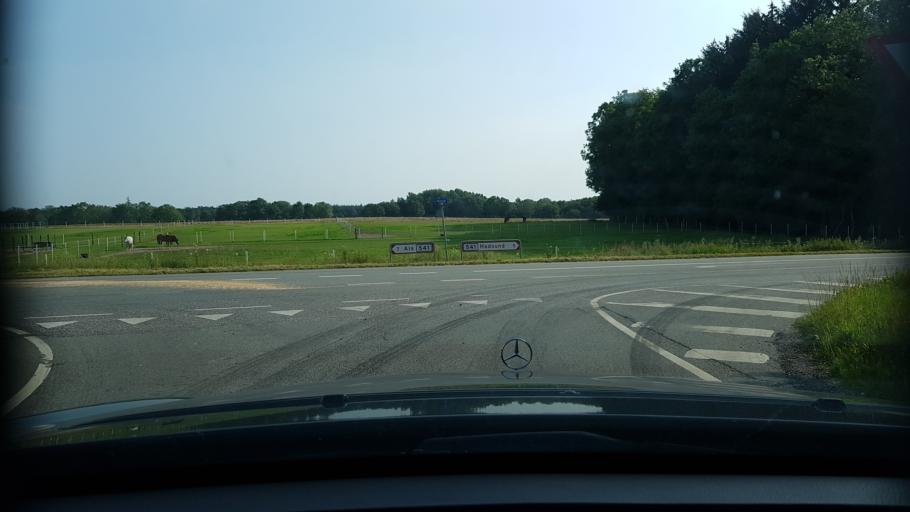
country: DK
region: North Denmark
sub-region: Mariagerfjord Kommune
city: Hadsund
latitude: 56.7445
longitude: 10.1775
